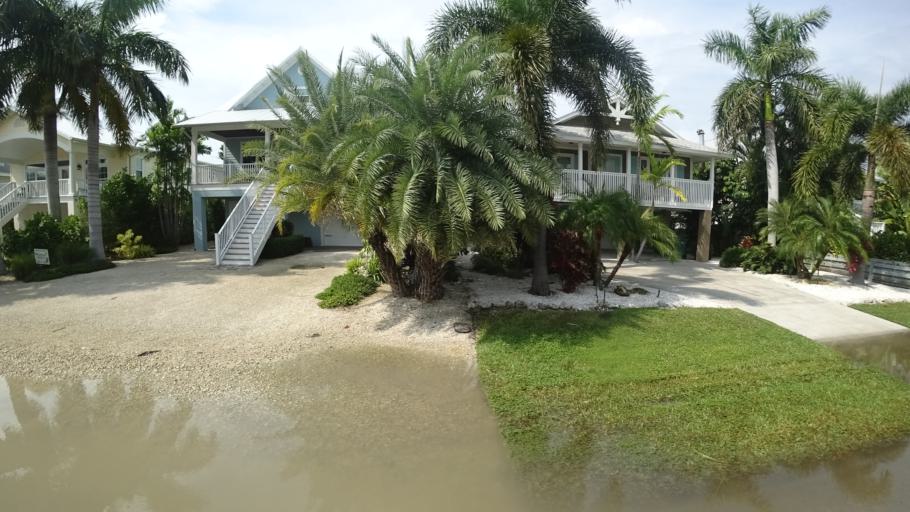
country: US
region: Florida
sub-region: Manatee County
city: Anna Maria
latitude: 27.5307
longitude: -82.7310
